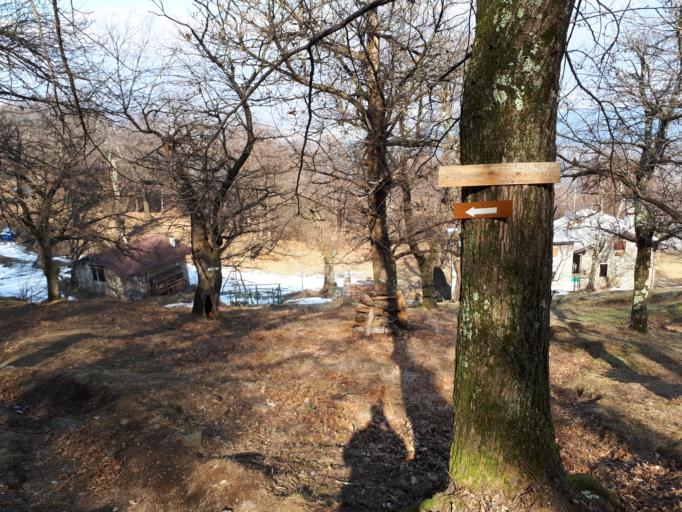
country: IT
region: Lombardy
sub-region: Provincia di Lecco
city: Sueglio
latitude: 46.1106
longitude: 9.3438
